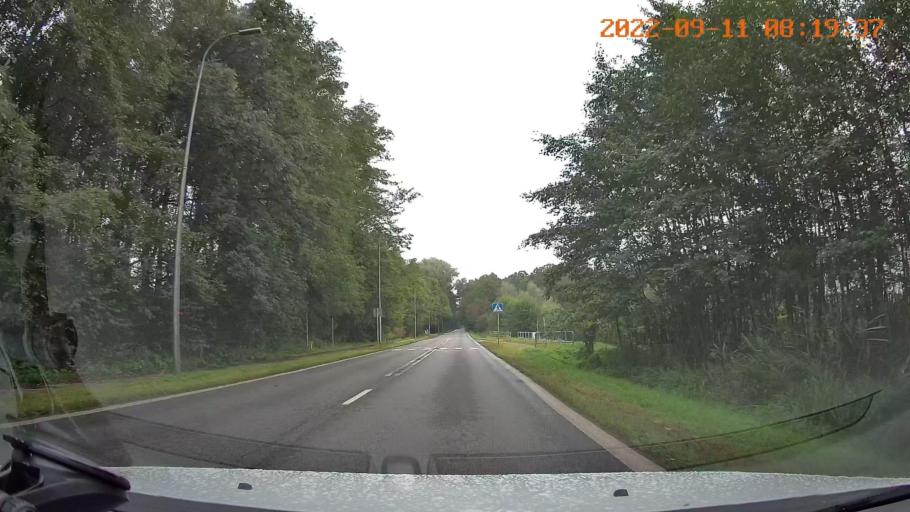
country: PL
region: Silesian Voivodeship
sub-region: Tychy
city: Tychy
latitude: 50.1528
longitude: 19.0066
